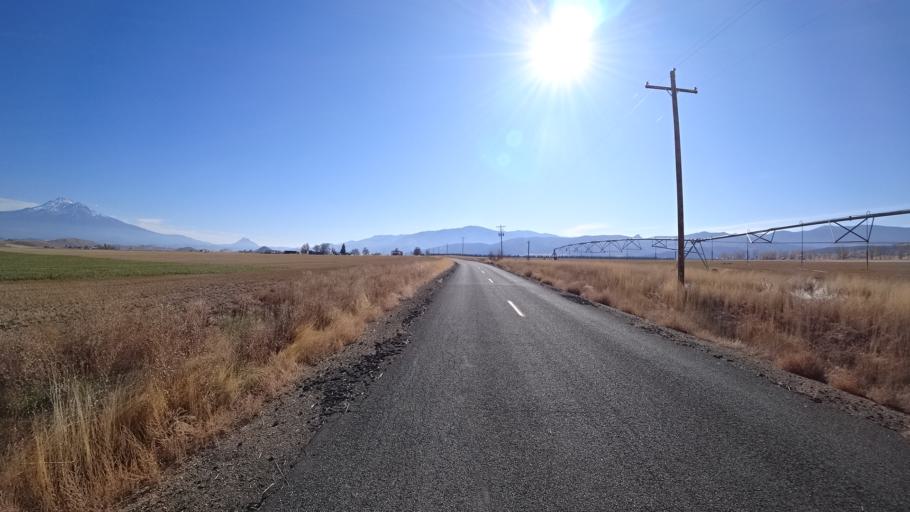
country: US
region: California
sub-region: Siskiyou County
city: Montague
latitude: 41.5643
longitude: -122.5481
